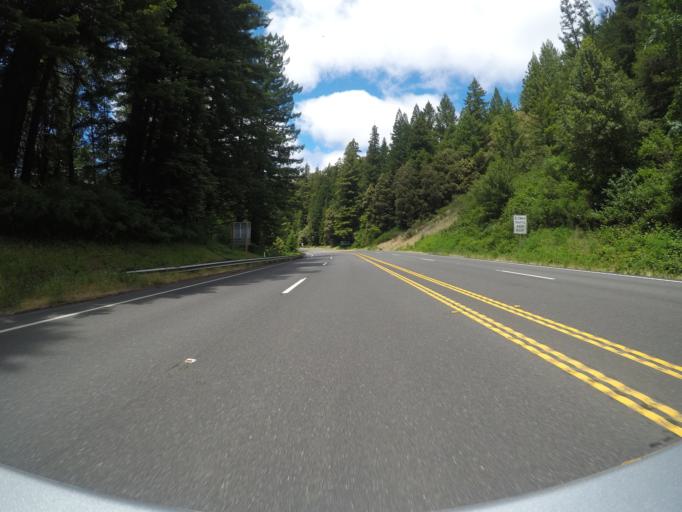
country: US
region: California
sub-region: Humboldt County
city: Redway
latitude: 40.2701
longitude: -123.8746
